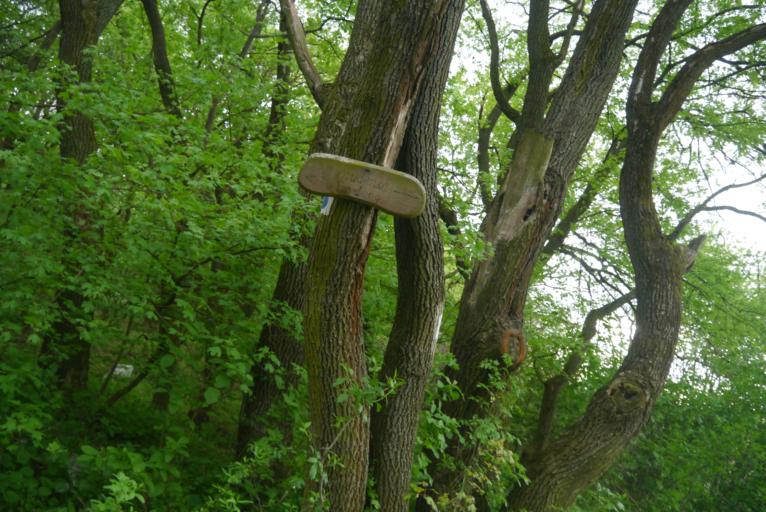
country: HU
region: Komarom-Esztergom
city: Piliscsev
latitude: 47.6765
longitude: 18.8374
